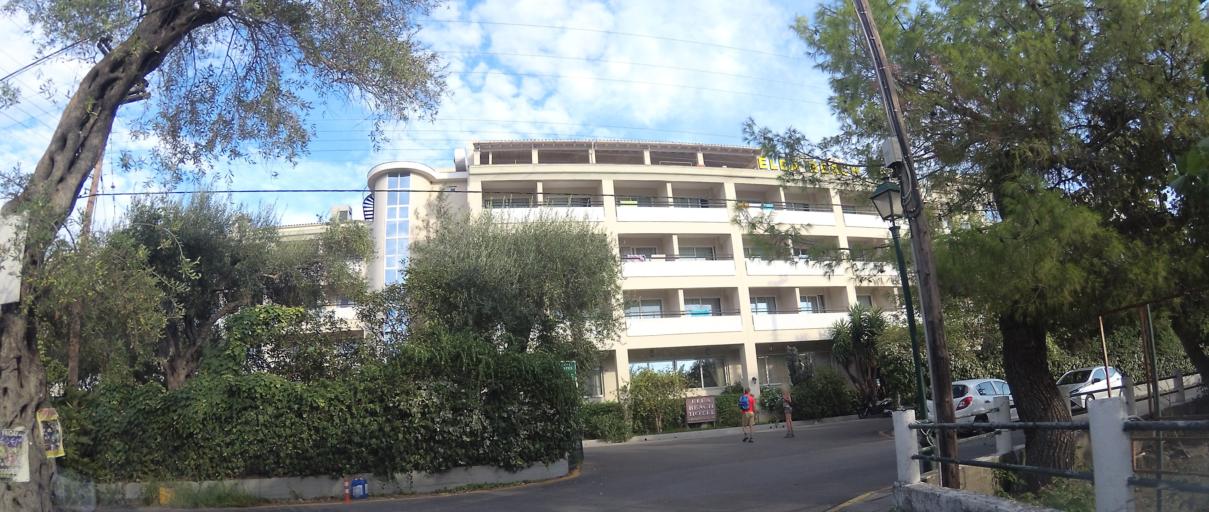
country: GR
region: Ionian Islands
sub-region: Nomos Kerkyras
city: Kontokali
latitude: 39.6843
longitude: 19.8410
